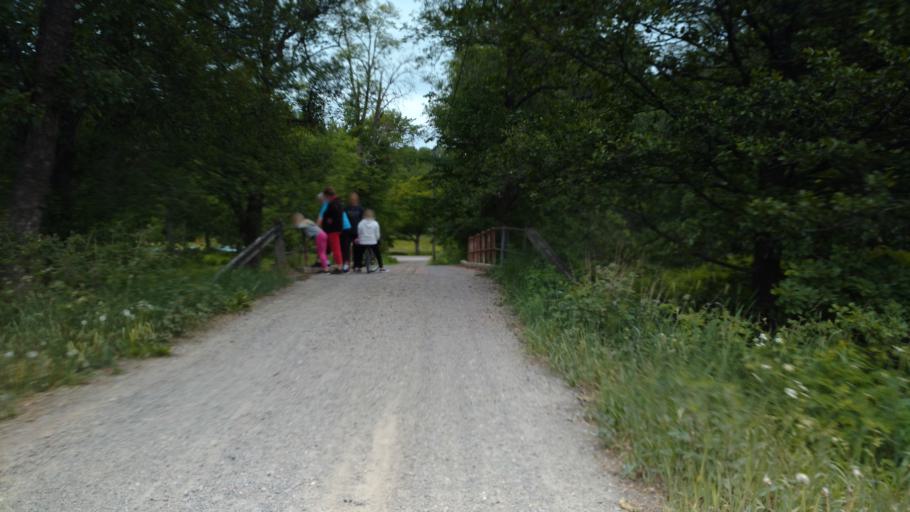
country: FI
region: Uusimaa
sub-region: Raaseporin
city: Pohja
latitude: 60.1243
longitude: 23.5373
